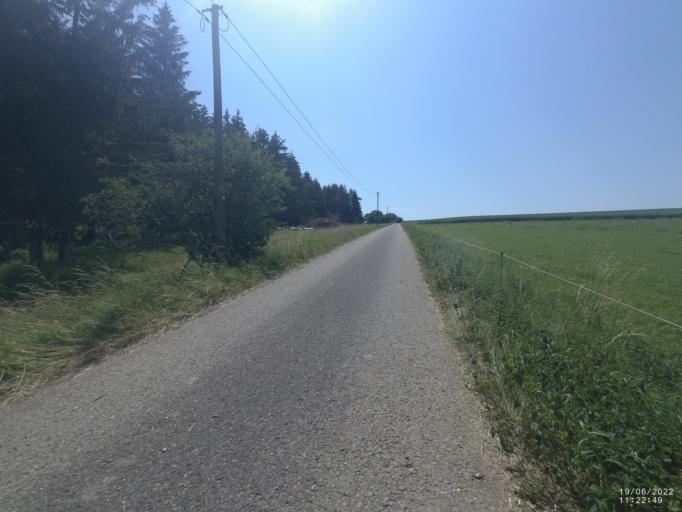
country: DE
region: Baden-Wuerttemberg
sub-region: Tuebingen Region
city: Weidenstetten
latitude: 48.6089
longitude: 9.9787
